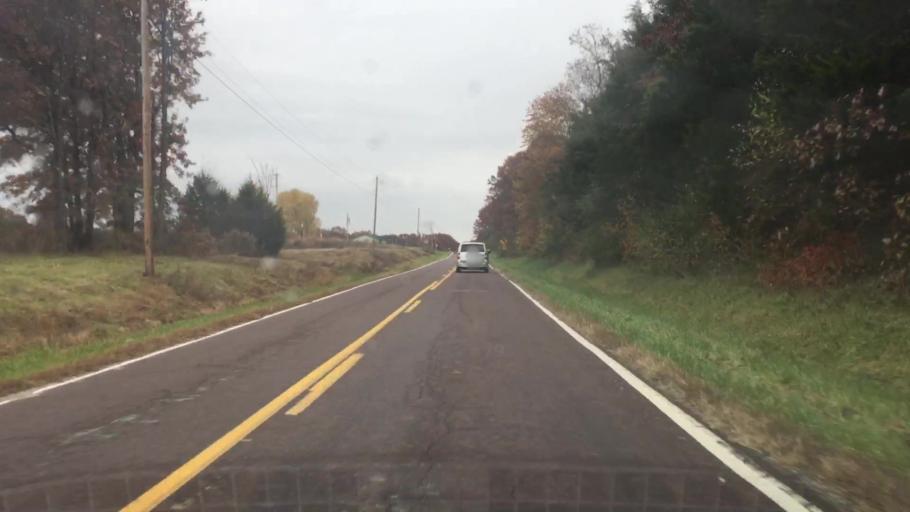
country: US
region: Missouri
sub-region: Callaway County
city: Fulton
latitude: 38.7871
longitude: -91.7672
